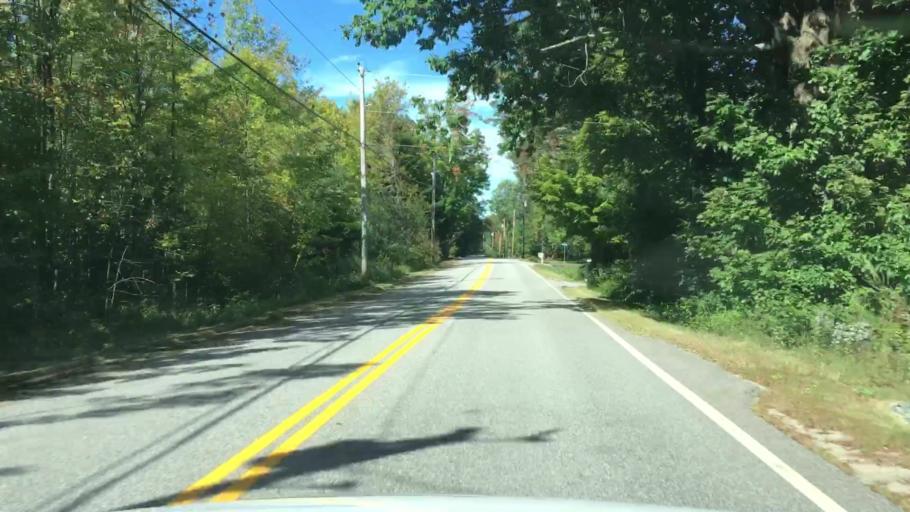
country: US
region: Maine
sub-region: Cumberland County
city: West Scarborough
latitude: 43.6203
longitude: -70.4069
